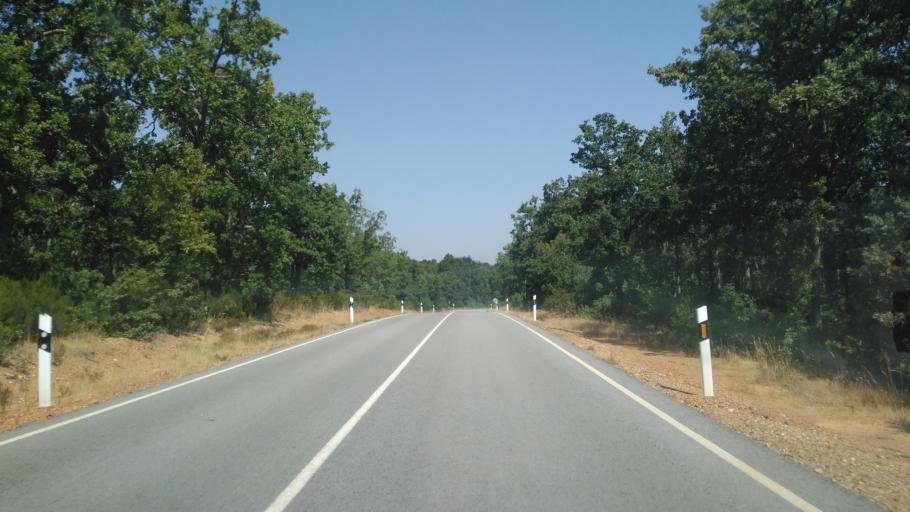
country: ES
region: Castille and Leon
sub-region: Provincia de Salamanca
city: Nava de Francia
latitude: 40.5496
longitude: -6.1350
